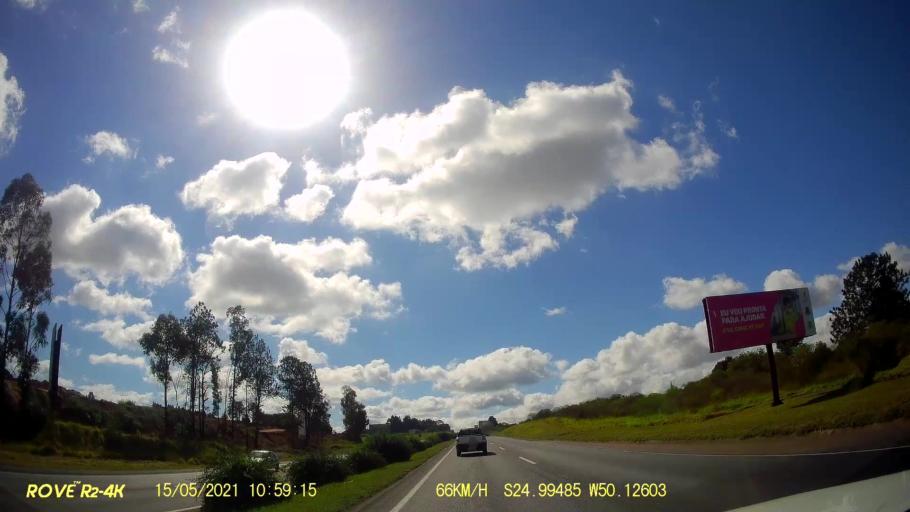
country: BR
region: Parana
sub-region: Carambei
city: Carambei
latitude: -24.9948
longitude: -50.1261
